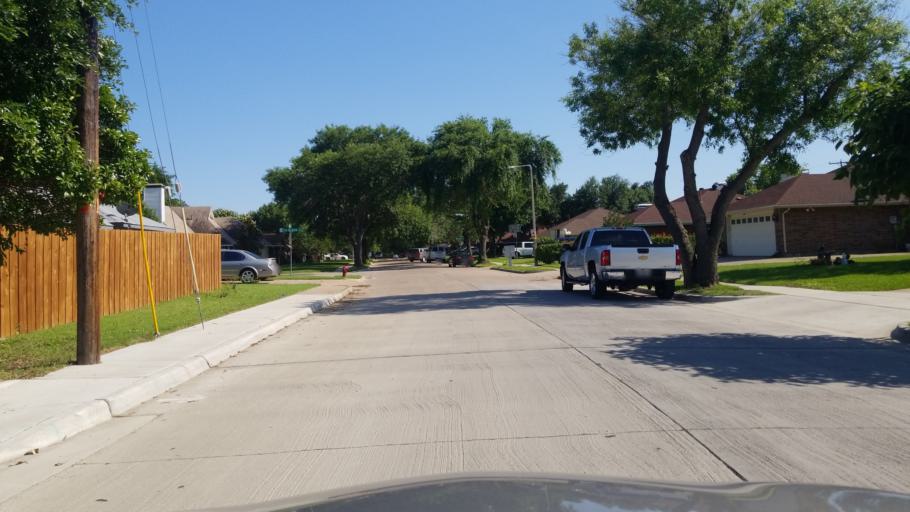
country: US
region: Texas
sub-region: Dallas County
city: Grand Prairie
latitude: 32.6843
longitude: -97.0114
